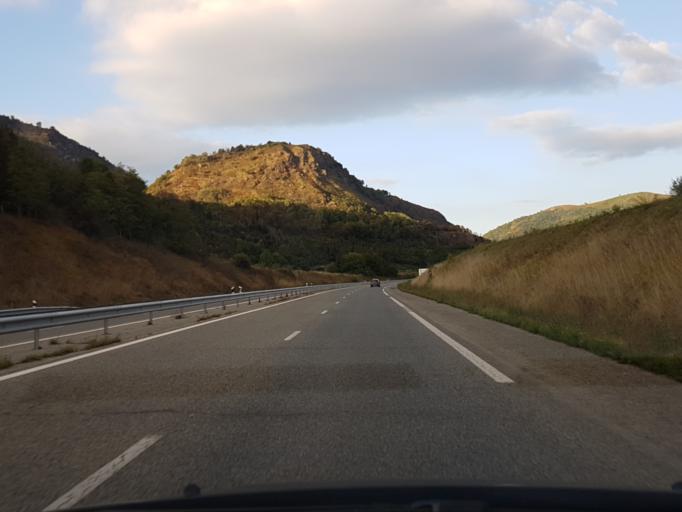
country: FR
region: Midi-Pyrenees
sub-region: Departement de l'Ariege
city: Tarascon-sur-Ariege
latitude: 42.8659
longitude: 1.6047
